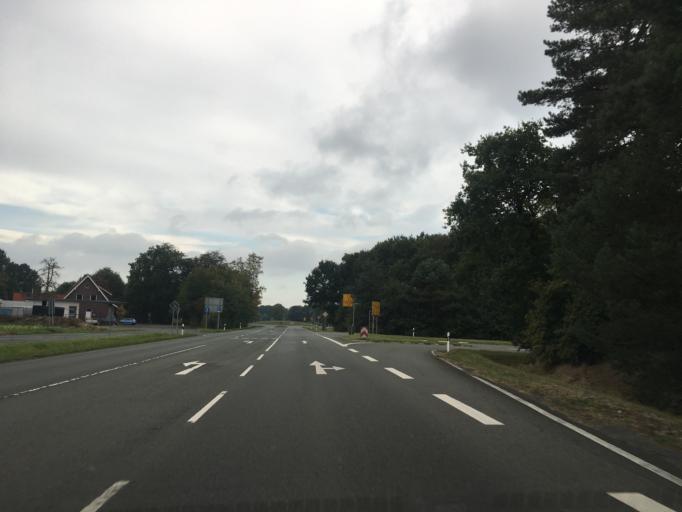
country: DE
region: North Rhine-Westphalia
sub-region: Regierungsbezirk Munster
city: Schoppingen
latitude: 52.1029
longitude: 7.2033
